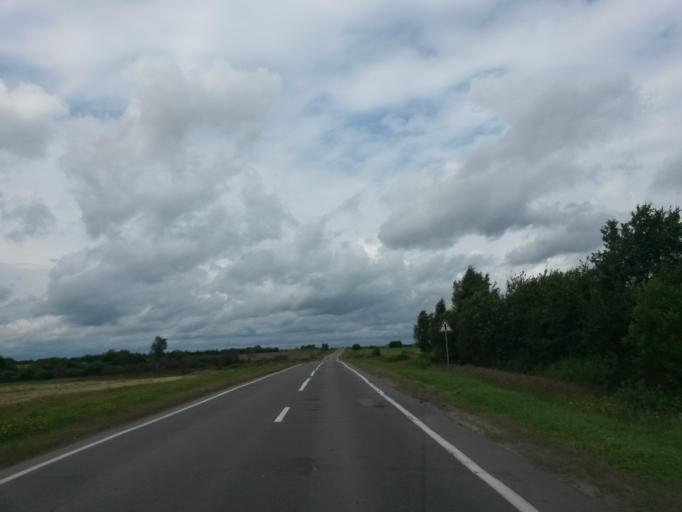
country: RU
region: Jaroslavl
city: Yaroslavl
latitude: 57.7463
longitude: 39.8832
